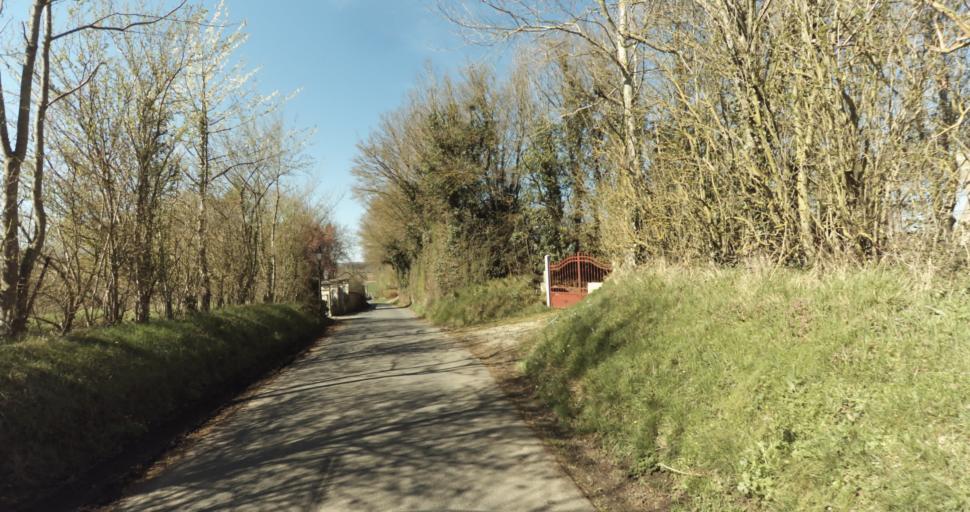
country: FR
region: Lower Normandy
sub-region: Departement du Calvados
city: Saint-Pierre-sur-Dives
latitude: 49.0509
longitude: -0.0204
